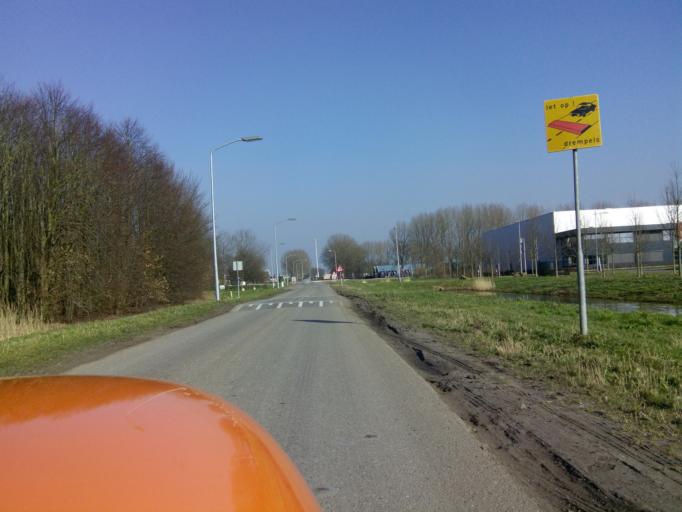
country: NL
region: Flevoland
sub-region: Gemeente Zeewolde
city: Zeewolde
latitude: 52.3525
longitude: 5.4894
